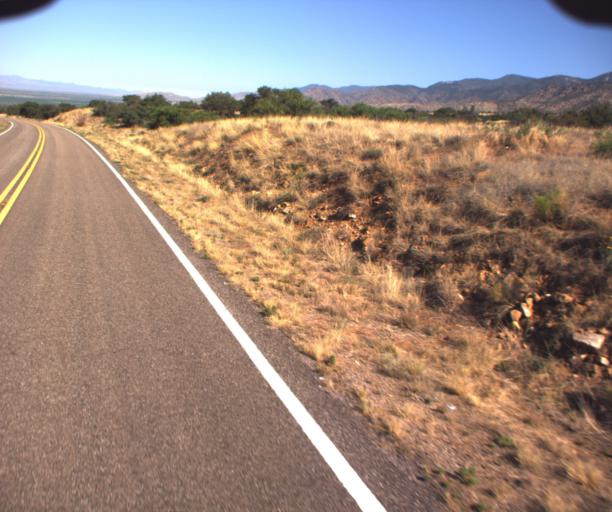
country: US
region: Arizona
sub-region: Graham County
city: Swift Trail Junction
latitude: 32.5999
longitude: -109.8786
